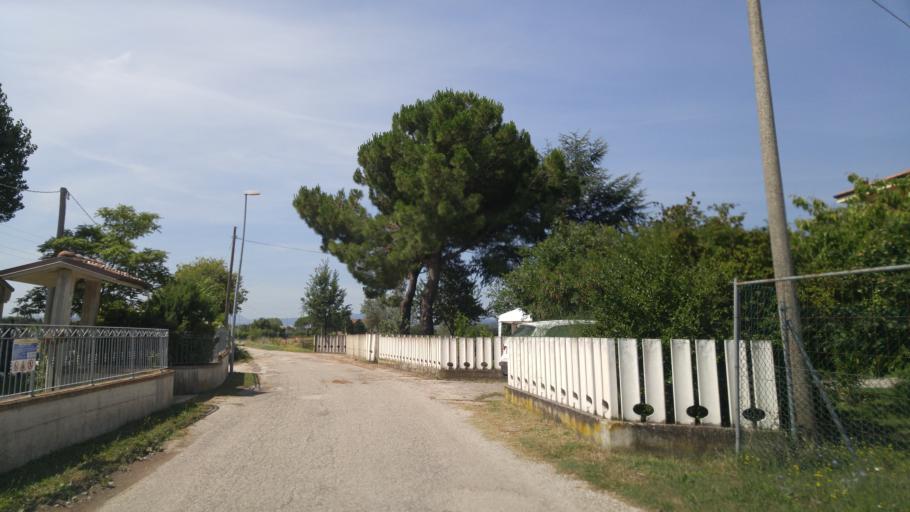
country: IT
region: The Marches
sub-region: Provincia di Pesaro e Urbino
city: Cuccurano
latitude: 43.7925
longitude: 12.9661
